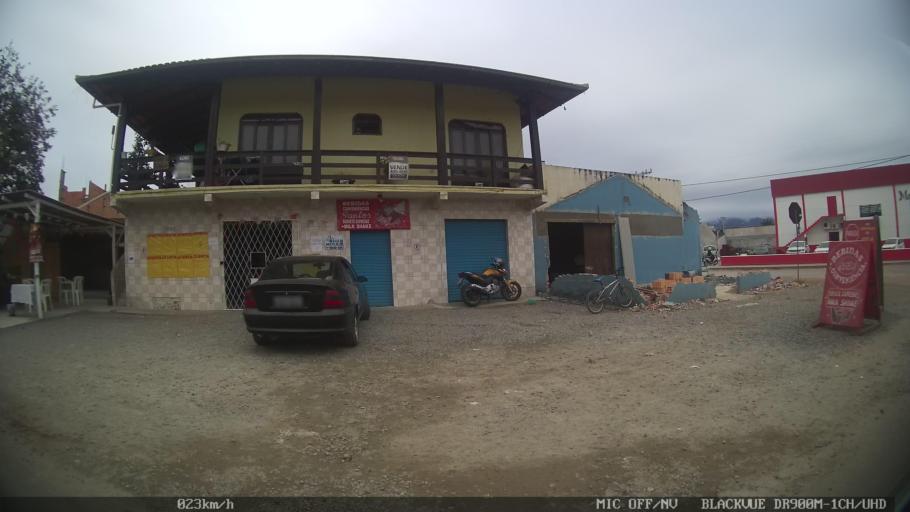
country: BR
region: Santa Catarina
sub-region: Joinville
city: Joinville
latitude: -26.3267
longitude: -48.9082
